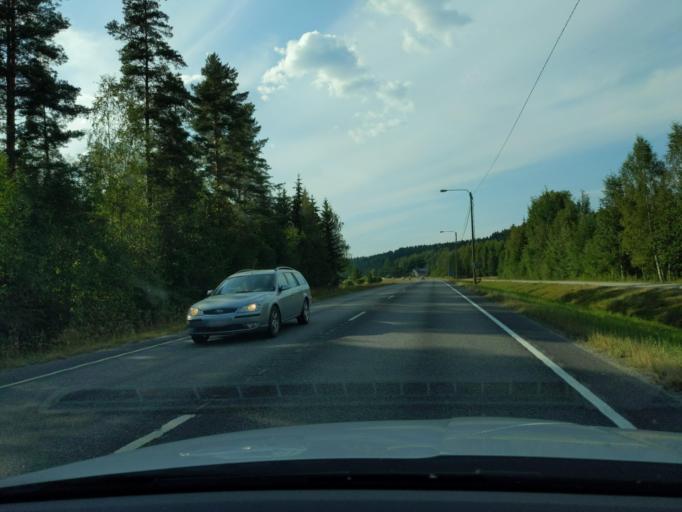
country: FI
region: Paijanne Tavastia
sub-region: Lahti
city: Asikkala
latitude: 61.1560
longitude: 25.5900
